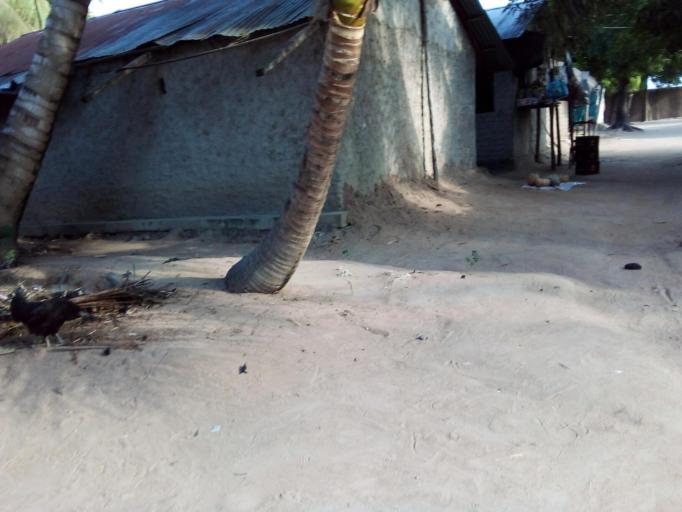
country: MZ
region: Zambezia
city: Quelimane
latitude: -17.6047
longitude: 36.8239
